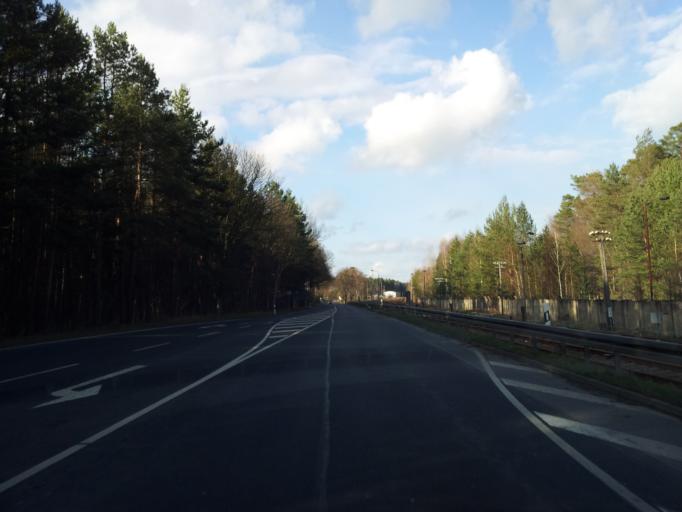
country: DE
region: Saxony
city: Ottendorf-Okrilla
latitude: 51.2027
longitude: 13.8361
